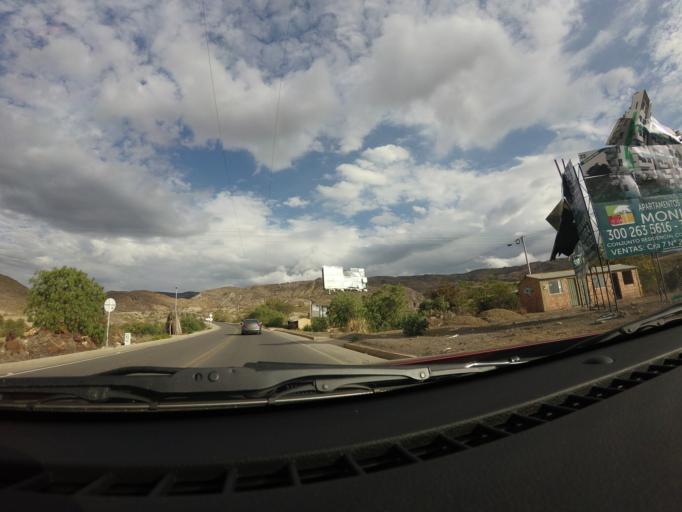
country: CO
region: Boyaca
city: Sachica
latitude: 5.5841
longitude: -73.5283
